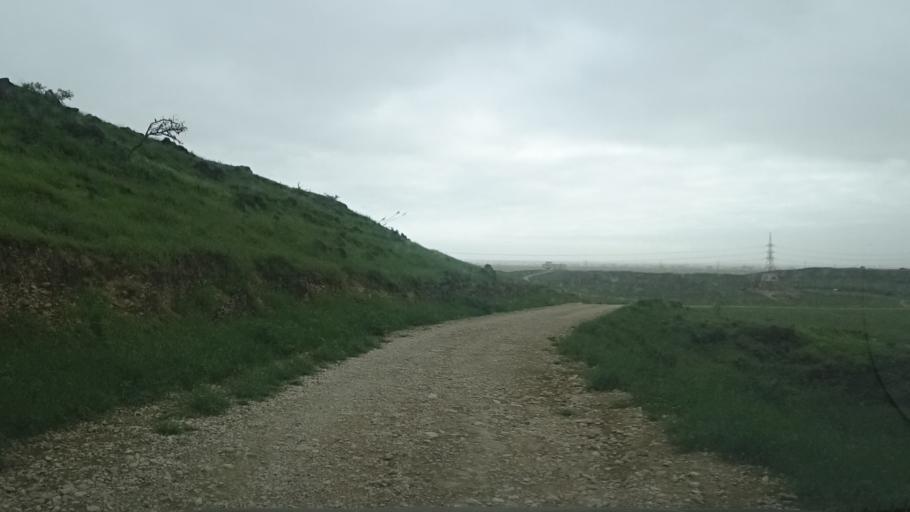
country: OM
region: Zufar
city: Salalah
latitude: 17.1144
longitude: 54.2390
